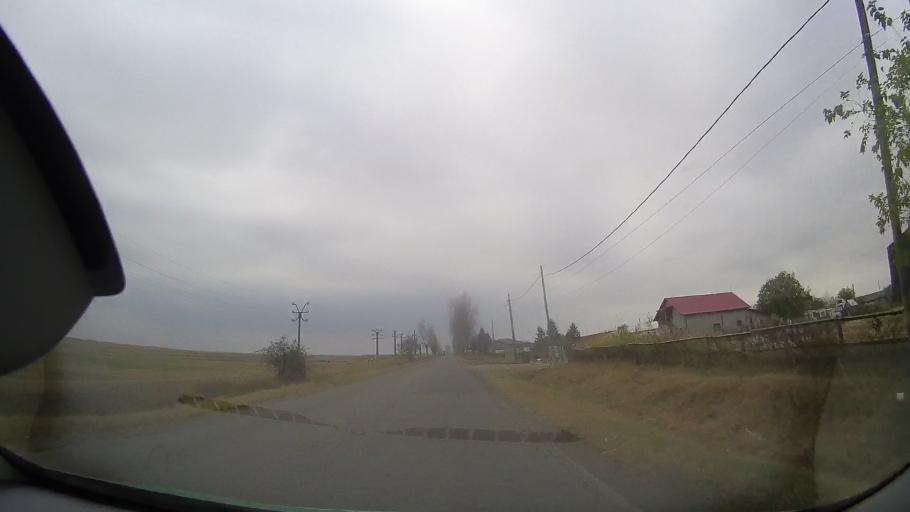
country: RO
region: Buzau
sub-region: Comuna Pogoanele
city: Pogoanele
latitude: 44.9016
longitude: 26.9770
